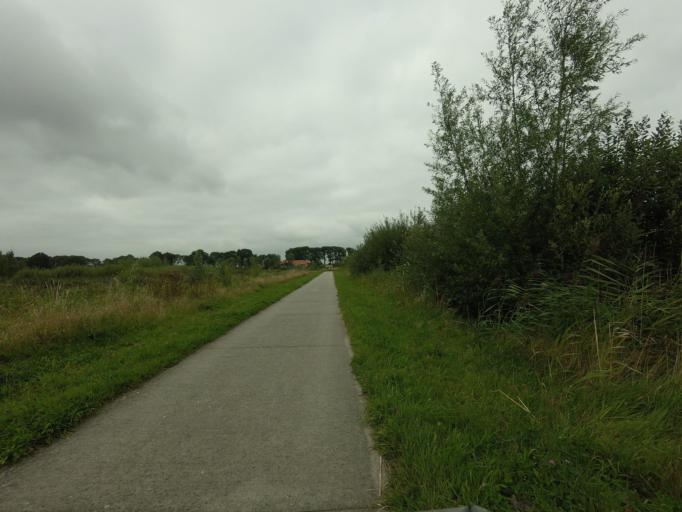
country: NL
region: Overijssel
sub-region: Gemeente Steenwijkerland
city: Giethoorn
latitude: 52.7190
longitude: 6.0628
